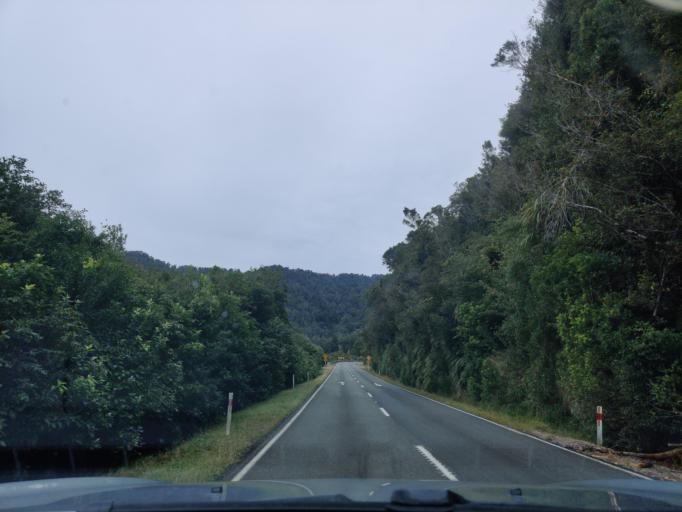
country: NZ
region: West Coast
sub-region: Buller District
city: Westport
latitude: -41.8616
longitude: 171.7723
